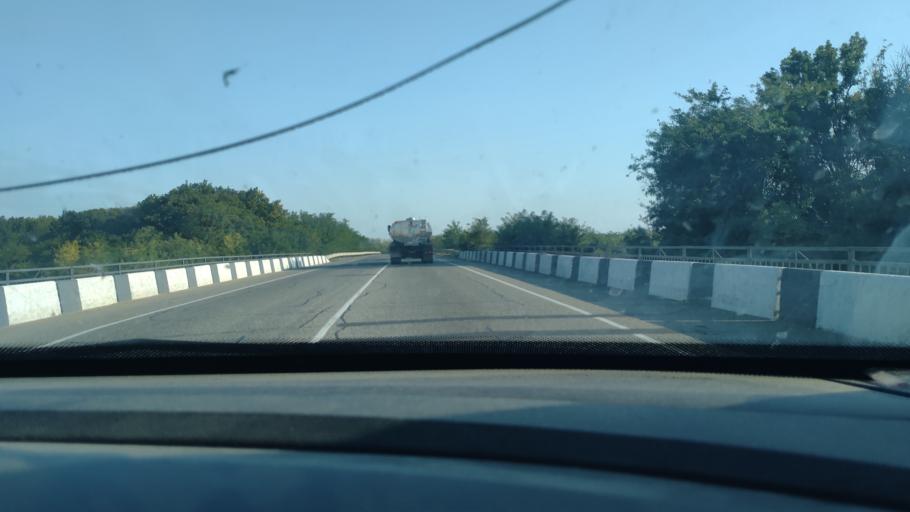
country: RU
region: Krasnodarskiy
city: Starominskaya
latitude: 46.5222
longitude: 39.0148
